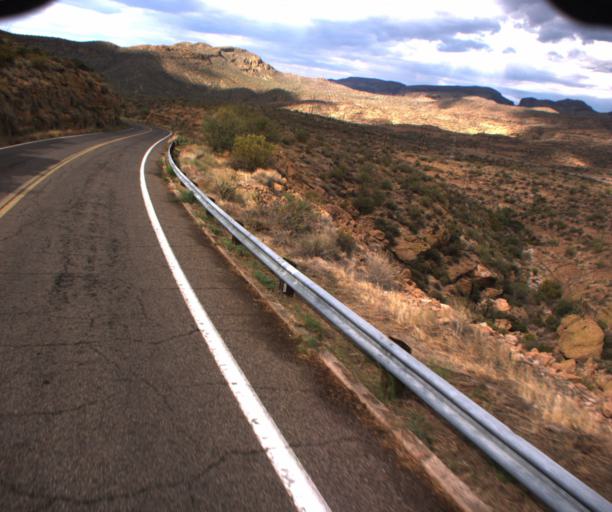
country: US
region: Arizona
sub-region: Pinal County
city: Apache Junction
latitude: 33.5330
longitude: -111.3592
